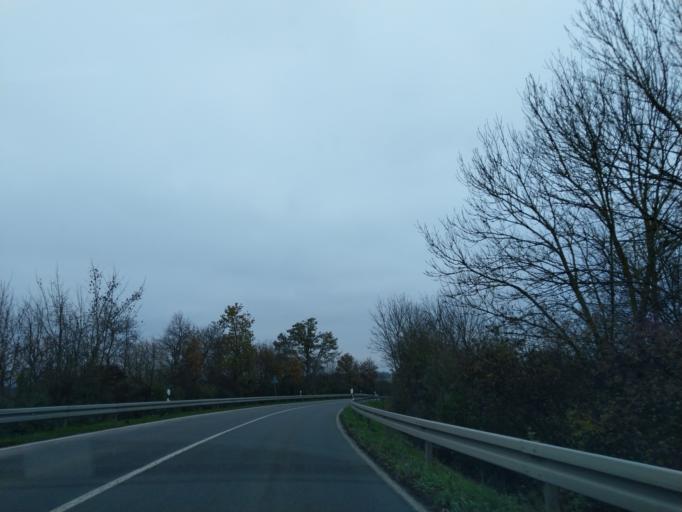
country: DE
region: Bavaria
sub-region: Lower Bavaria
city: Otzing
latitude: 48.7774
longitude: 12.7929
